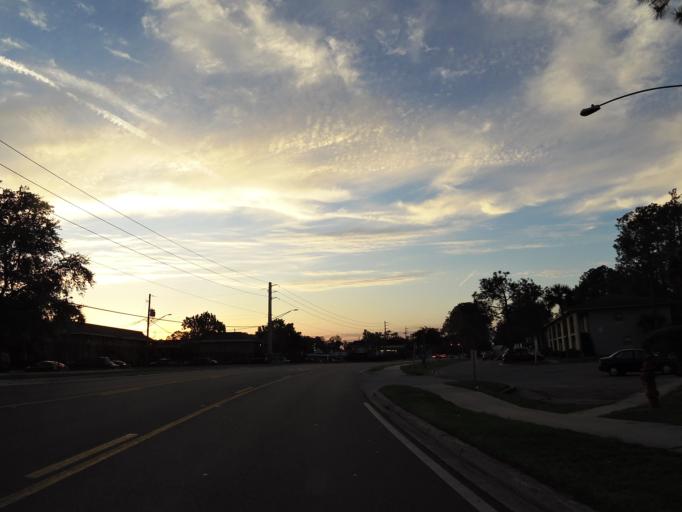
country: US
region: Florida
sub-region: Duval County
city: Jacksonville
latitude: 30.2708
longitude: -81.6066
